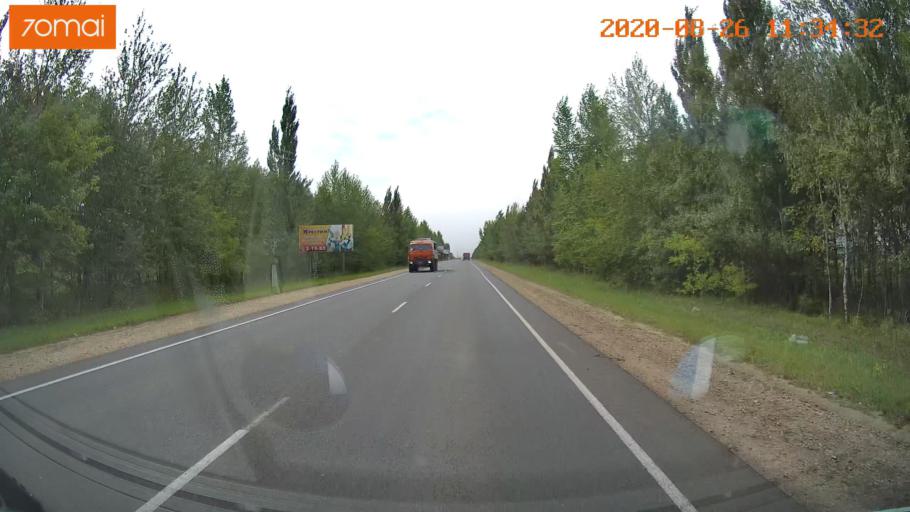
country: RU
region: Rjazan
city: Shilovo
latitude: 54.2847
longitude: 40.8428
